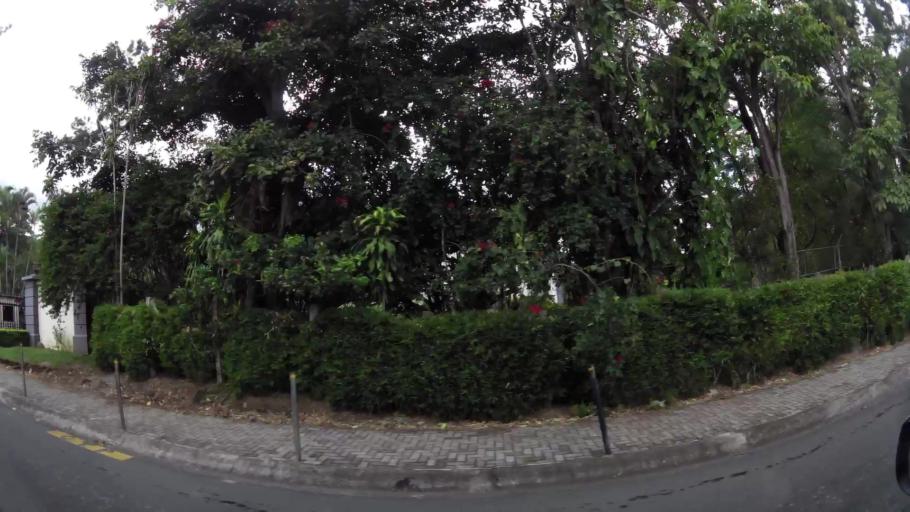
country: CR
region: San Jose
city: Escazu
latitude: 9.9235
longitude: -84.1452
